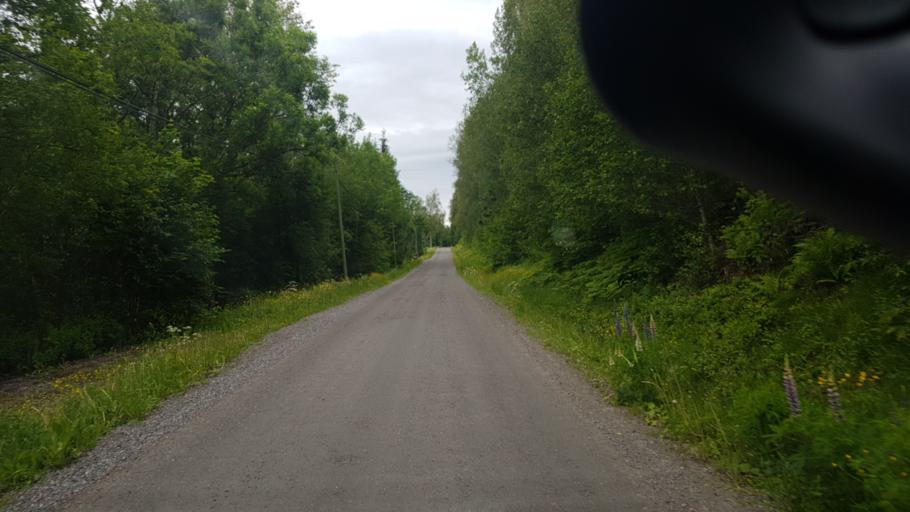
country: SE
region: Vaermland
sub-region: Eda Kommun
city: Amotfors
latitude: 59.7441
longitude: 12.2760
